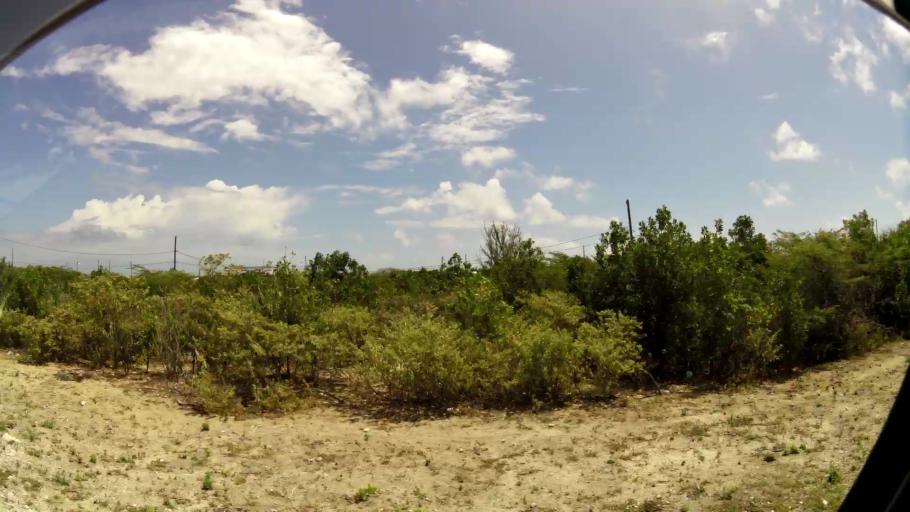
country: TC
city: Cockburn Town
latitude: 21.4778
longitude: -71.1487
